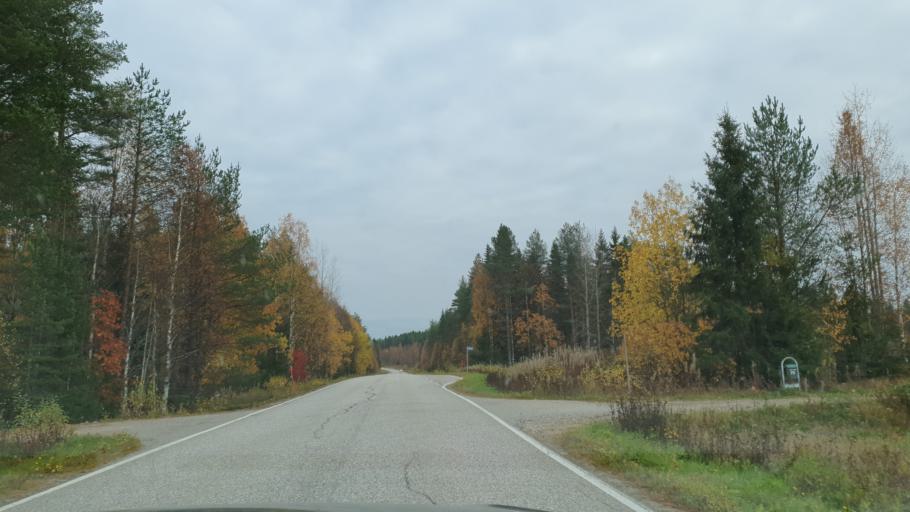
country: FI
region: Kainuu
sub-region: Kajaani
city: Ristijaervi
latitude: 64.4567
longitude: 28.3305
